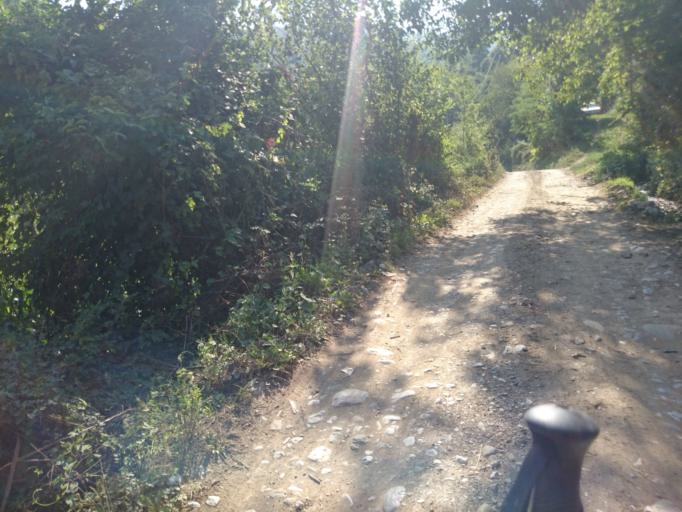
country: AL
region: Diber
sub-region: Rrethi i Dibres
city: Arras
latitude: 41.7378
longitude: 20.3024
